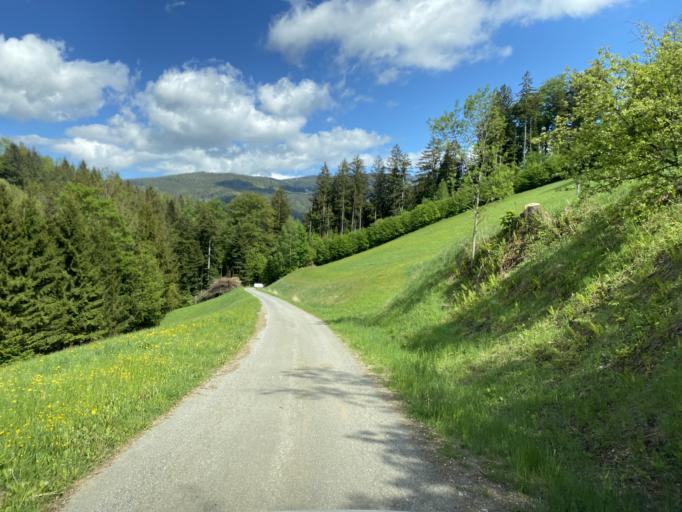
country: AT
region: Styria
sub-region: Politischer Bezirk Weiz
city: Koglhof
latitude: 47.3092
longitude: 15.6732
